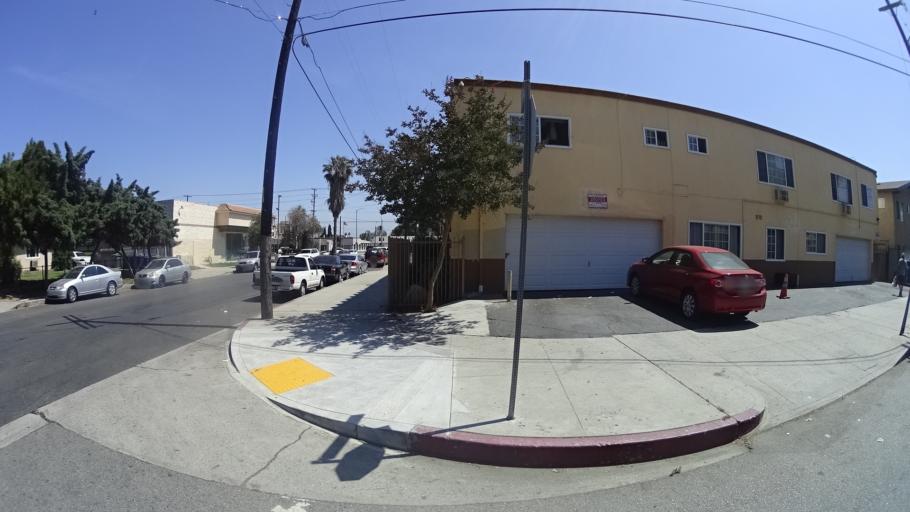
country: US
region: California
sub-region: Los Angeles County
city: Van Nuys
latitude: 34.2022
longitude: -118.4282
